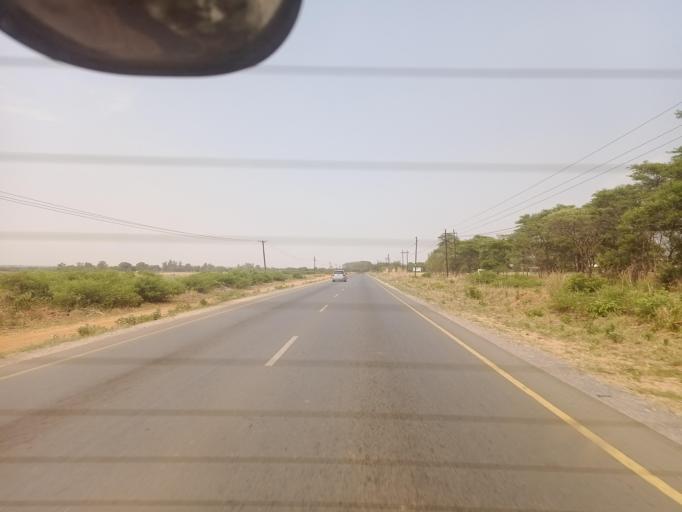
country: ZM
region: Lusaka
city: Lusaka
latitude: -15.2698
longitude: 28.4138
